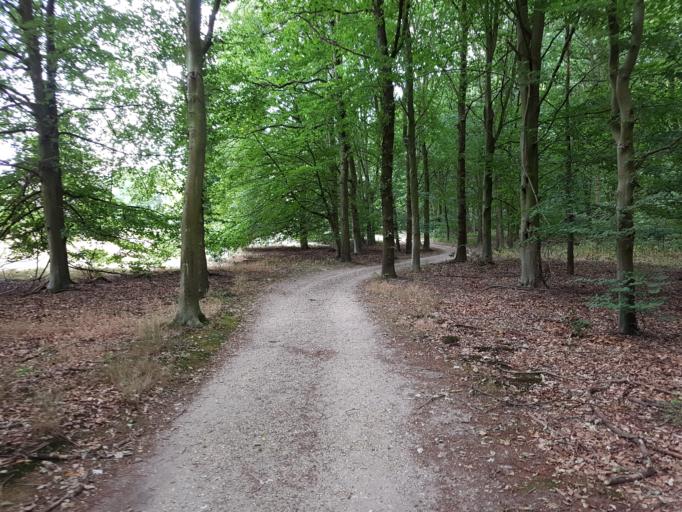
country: NL
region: Gelderland
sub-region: Gemeente Apeldoorn
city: Apeldoorn
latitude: 52.2386
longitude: 5.9399
